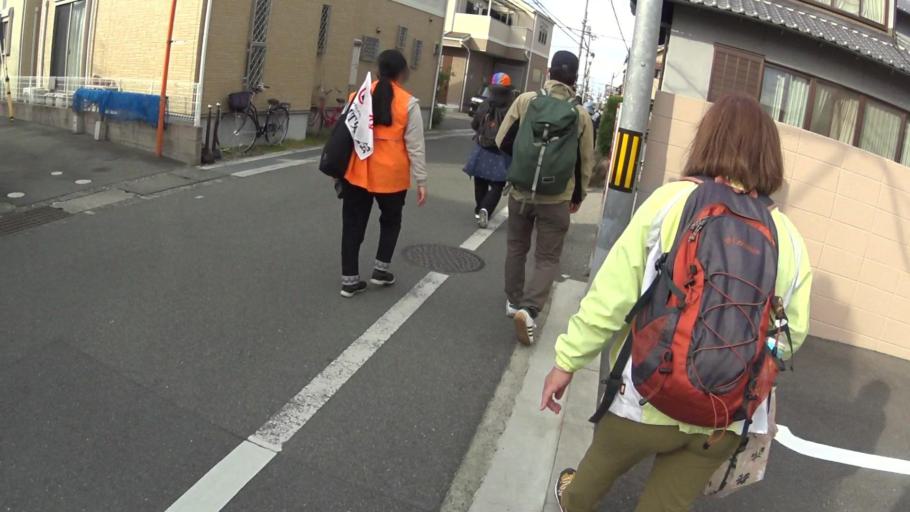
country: JP
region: Osaka
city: Kashihara
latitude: 34.5783
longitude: 135.5914
